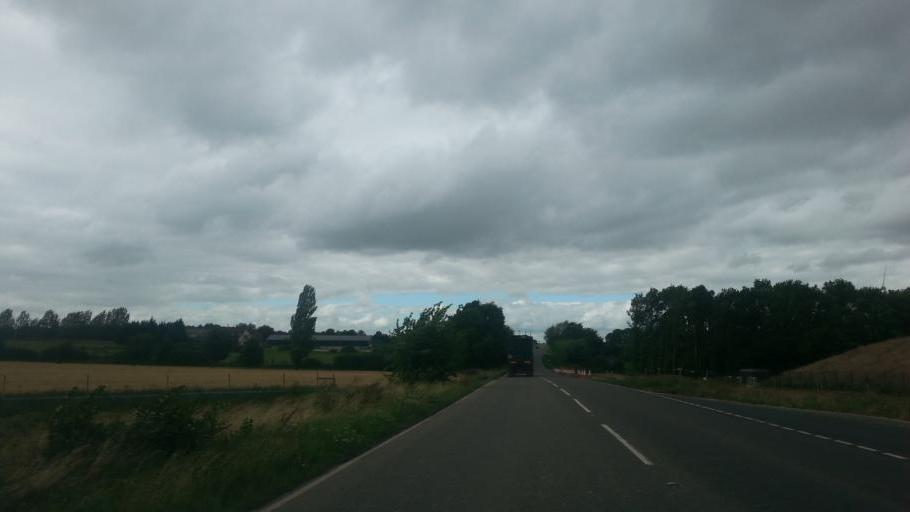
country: GB
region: England
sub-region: Cambridgeshire
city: Godmanchester
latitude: 52.2942
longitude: -0.1510
